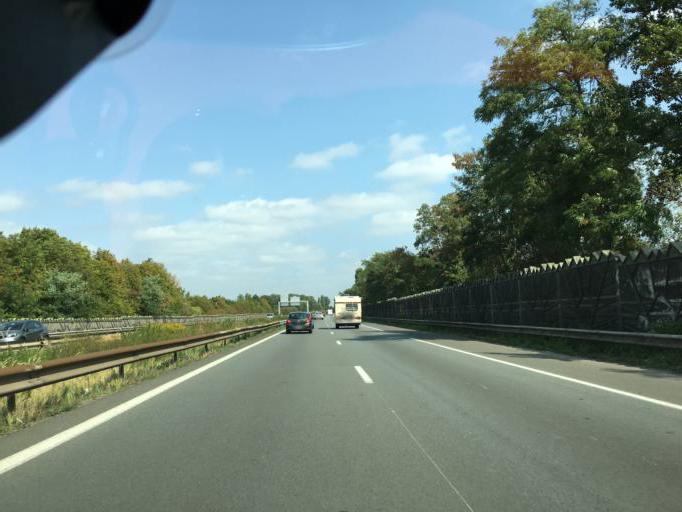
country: FR
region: Nord-Pas-de-Calais
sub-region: Departement du Nord
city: Douchy-les-Mines
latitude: 50.3078
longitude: 3.3839
